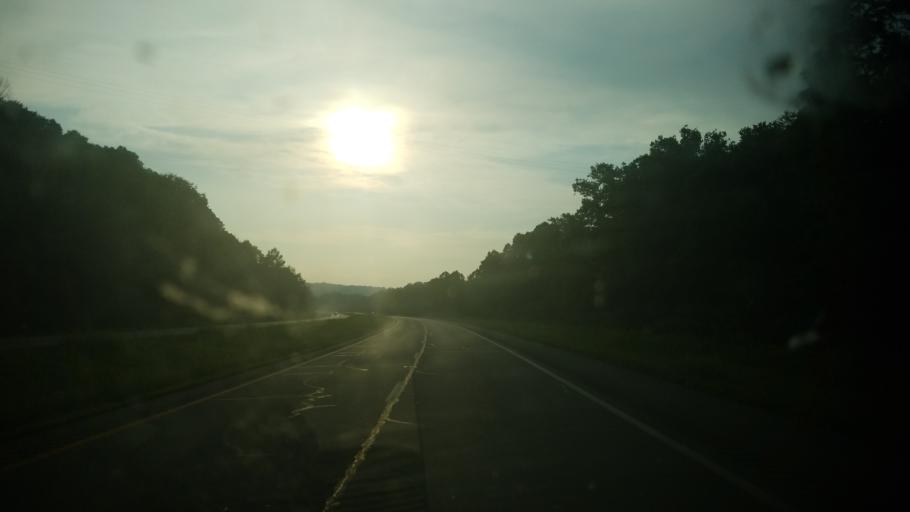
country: US
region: Ohio
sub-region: Pike County
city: Piketon
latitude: 39.0593
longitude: -83.0725
